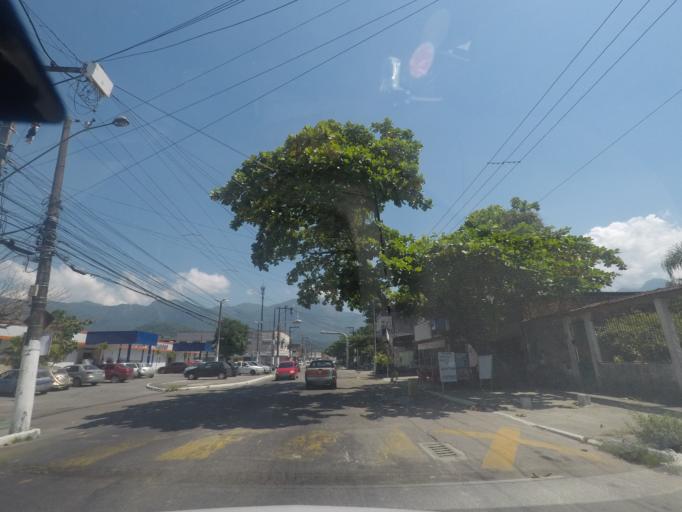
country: BR
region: Rio de Janeiro
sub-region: Petropolis
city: Petropolis
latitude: -22.5976
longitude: -43.1873
